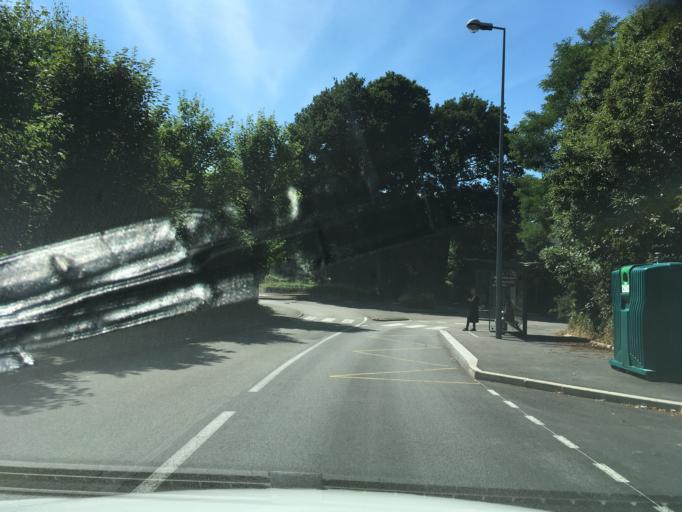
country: FR
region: Brittany
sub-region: Departement du Finistere
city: Quimper
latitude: 47.9759
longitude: -4.1296
